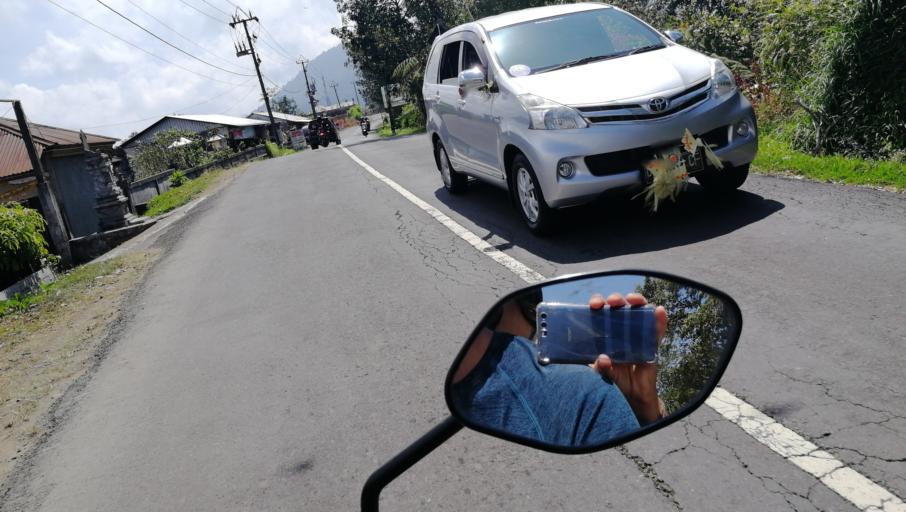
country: ID
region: Bali
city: Munduk
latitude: -8.2369
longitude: 115.1290
